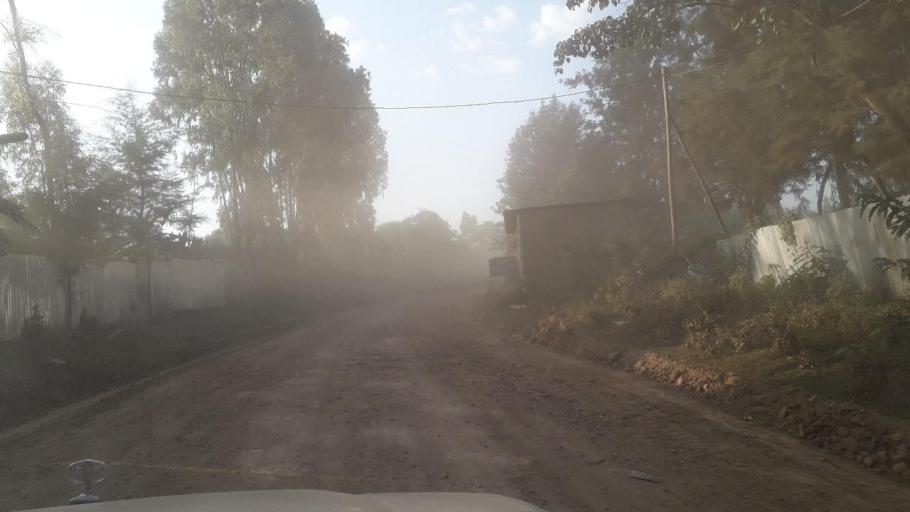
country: ET
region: Oromiya
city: Jima
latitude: 7.6266
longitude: 36.8302
